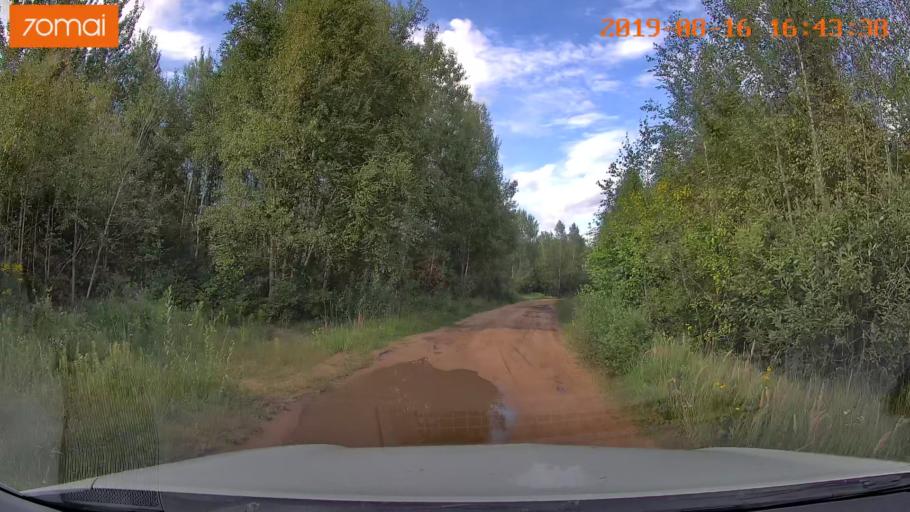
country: BY
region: Mogilev
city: Asipovichy
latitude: 53.2446
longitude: 28.7777
